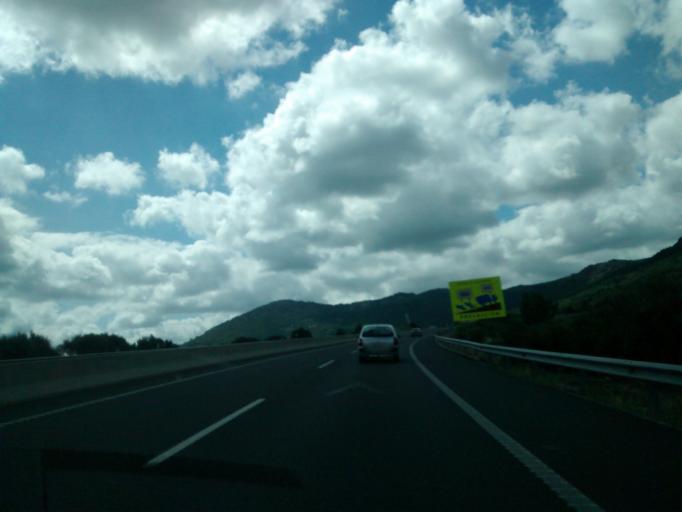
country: ES
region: Extremadura
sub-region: Provincia de Caceres
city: Higuera
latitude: 39.7088
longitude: -5.6916
